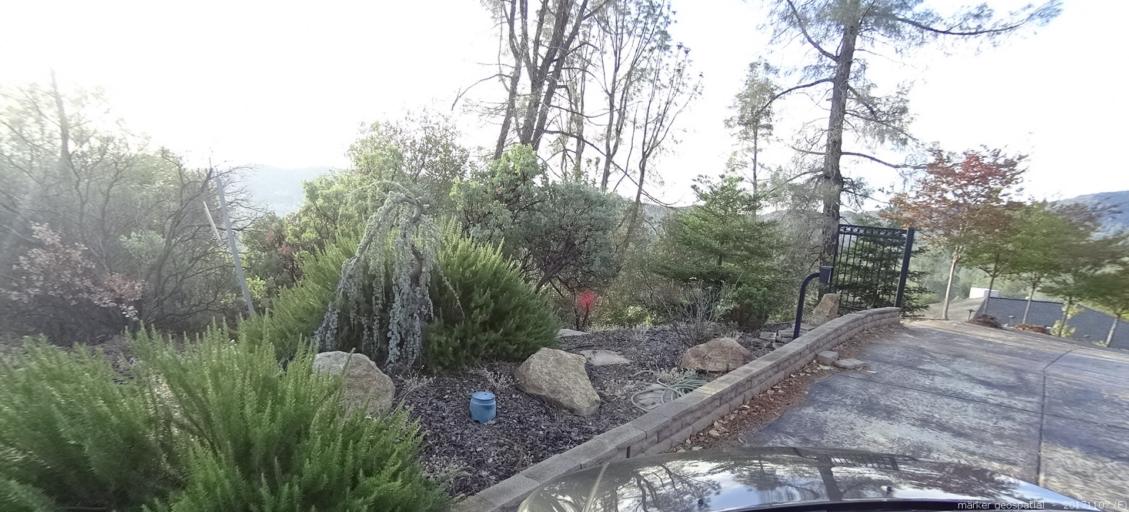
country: US
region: California
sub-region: Shasta County
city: Shasta
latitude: 40.5862
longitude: -122.4702
